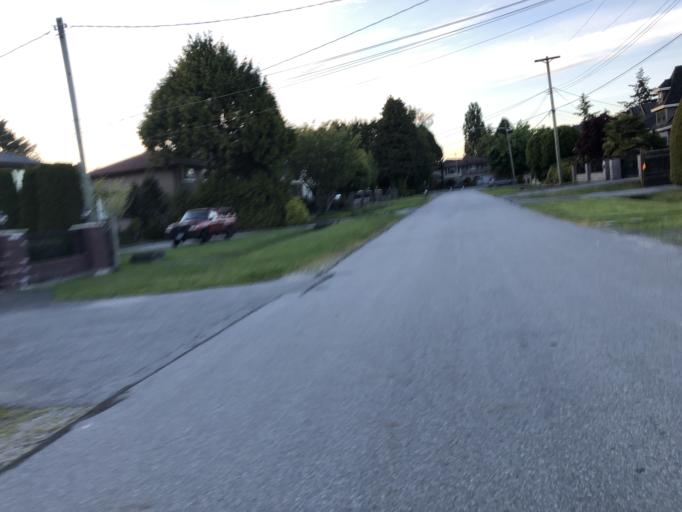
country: CA
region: British Columbia
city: Richmond
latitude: 49.1358
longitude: -123.1191
